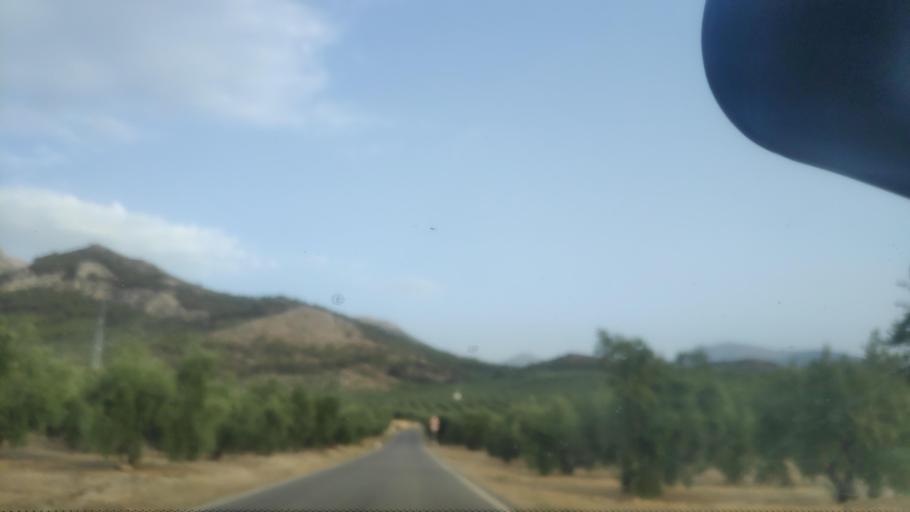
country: ES
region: Andalusia
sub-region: Provincia de Jaen
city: Torres
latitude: 37.8320
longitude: -3.5269
